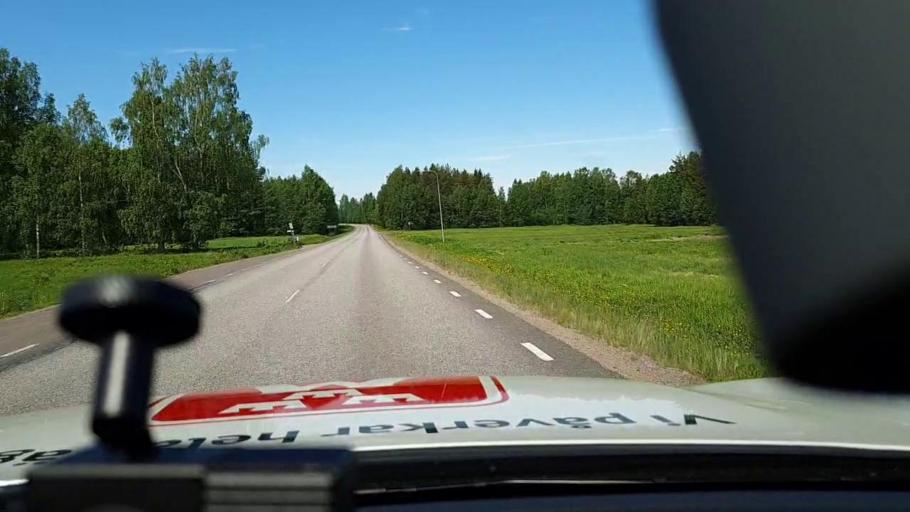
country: SE
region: Norrbotten
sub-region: Lulea Kommun
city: Sodra Sunderbyn
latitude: 65.6572
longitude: 21.8447
